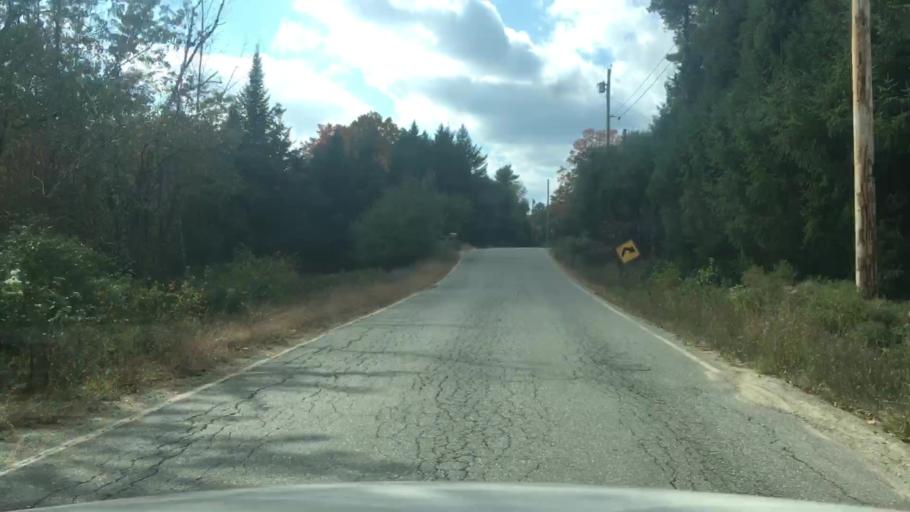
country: US
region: Maine
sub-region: Knox County
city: Washington
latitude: 44.3235
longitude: -69.3603
